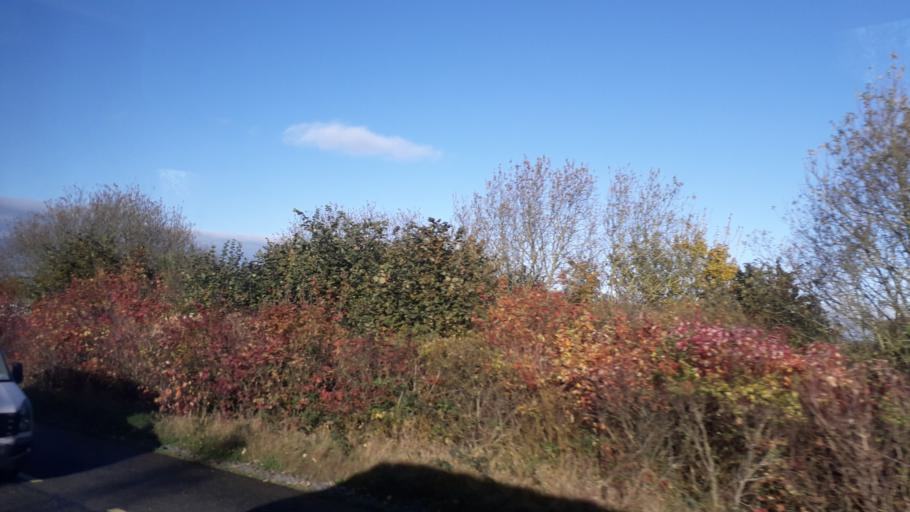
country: IE
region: Leinster
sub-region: Lu
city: Ardee
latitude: 53.8587
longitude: -6.5167
